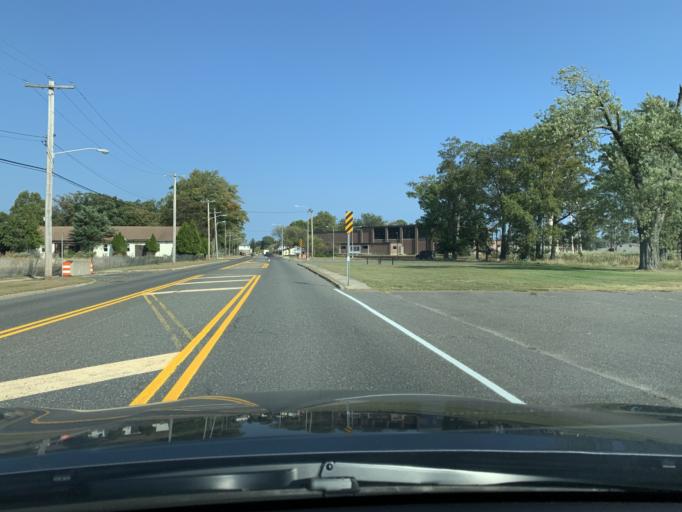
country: US
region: New Jersey
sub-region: Monmouth County
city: Eatontown
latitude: 40.3128
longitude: -74.0456
